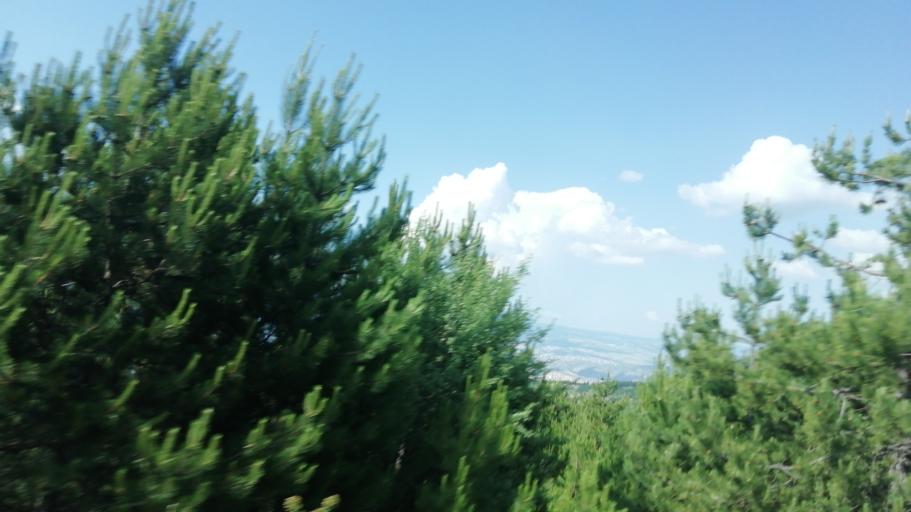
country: TR
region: Karabuk
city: Karabuk
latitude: 41.1250
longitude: 32.5819
